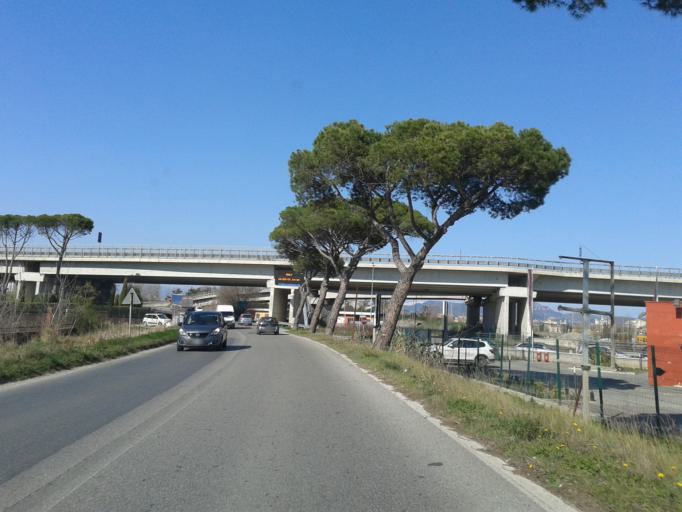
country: IT
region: Tuscany
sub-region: Province of Pisa
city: Pisa
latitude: 43.6988
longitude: 10.3890
